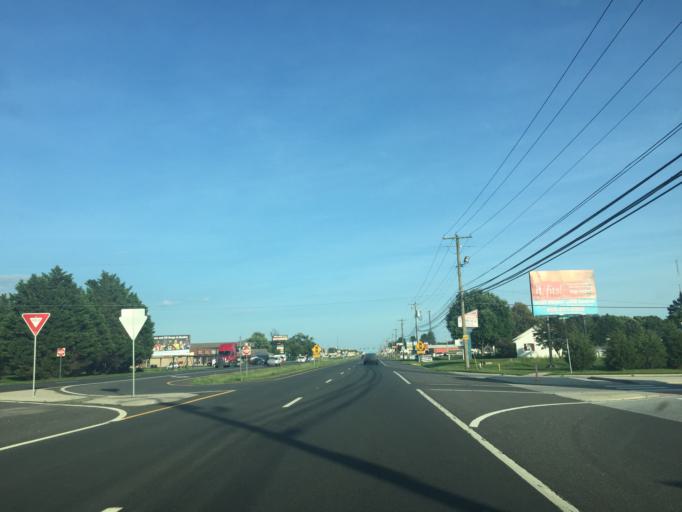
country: US
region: Delaware
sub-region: Kent County
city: Cheswold
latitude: 39.2090
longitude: -75.5685
